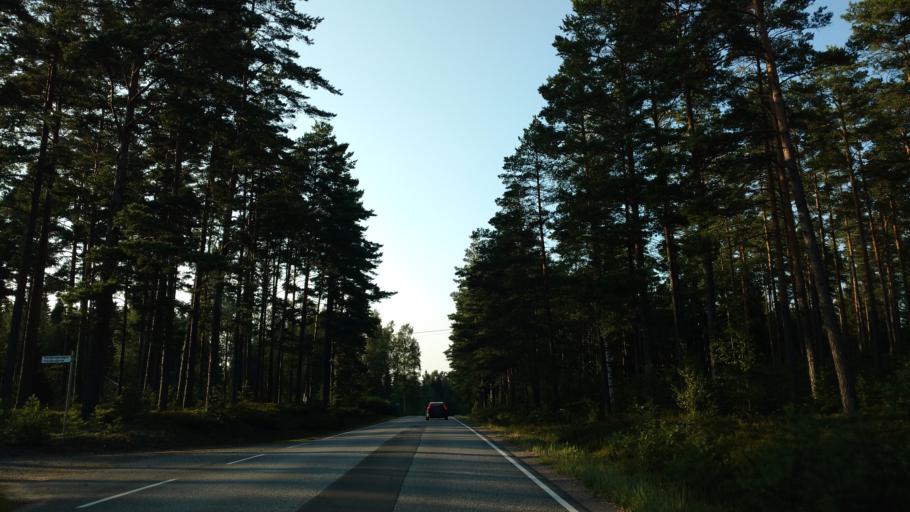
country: FI
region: Varsinais-Suomi
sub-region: Aboland-Turunmaa
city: Dragsfjaerd
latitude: 60.0669
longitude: 22.4506
